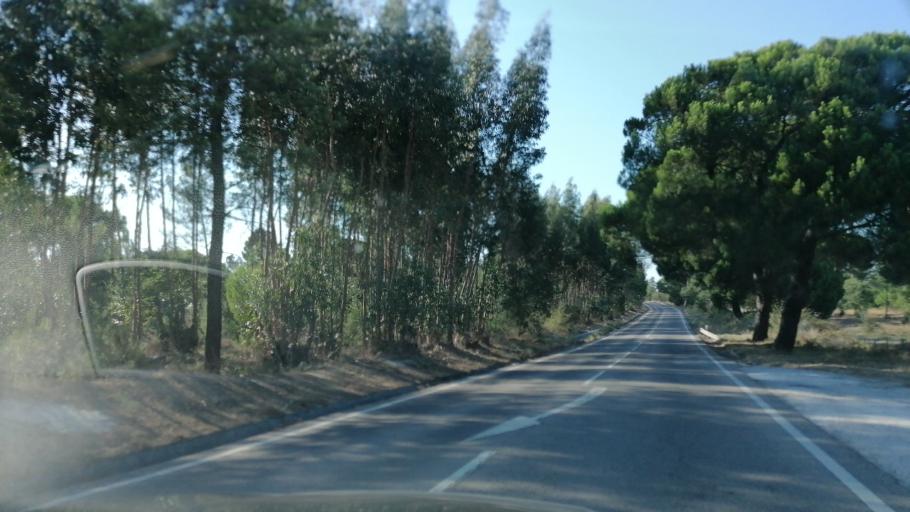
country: PT
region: Santarem
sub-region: Coruche
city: Coruche
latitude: 38.9803
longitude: -8.5456
